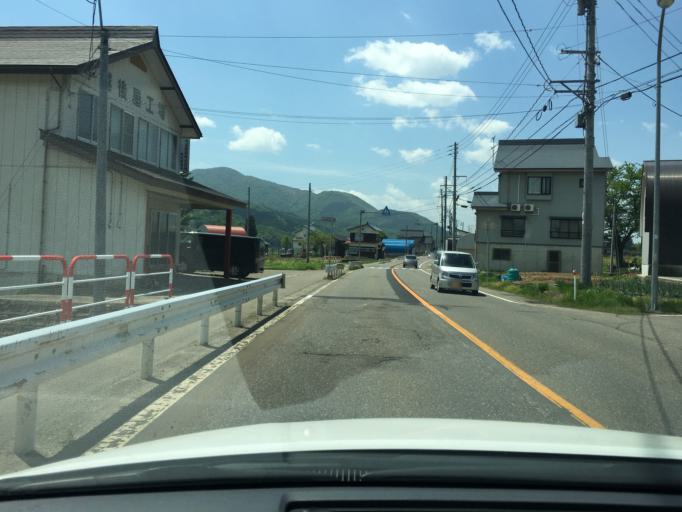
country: JP
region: Niigata
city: Tochio-honcho
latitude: 37.3289
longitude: 139.0264
